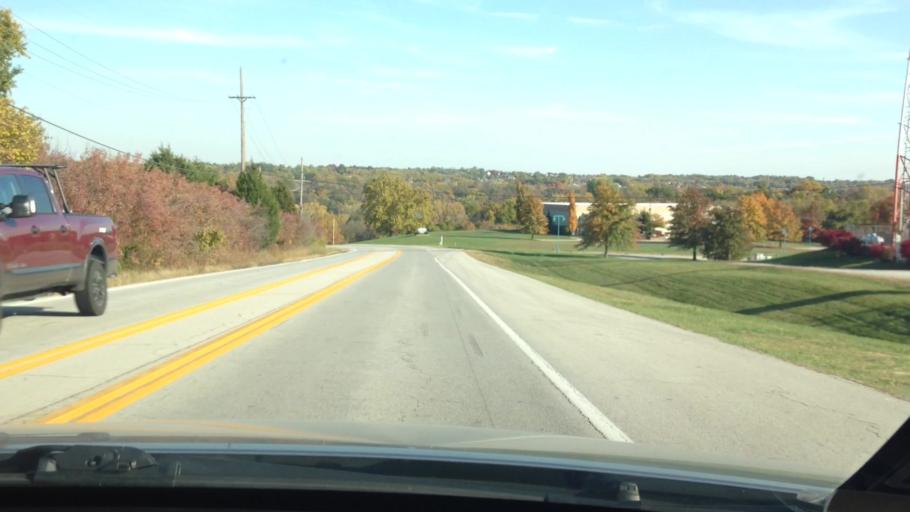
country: US
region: Missouri
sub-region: Platte County
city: Weatherby Lake
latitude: 39.2254
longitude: -94.7701
